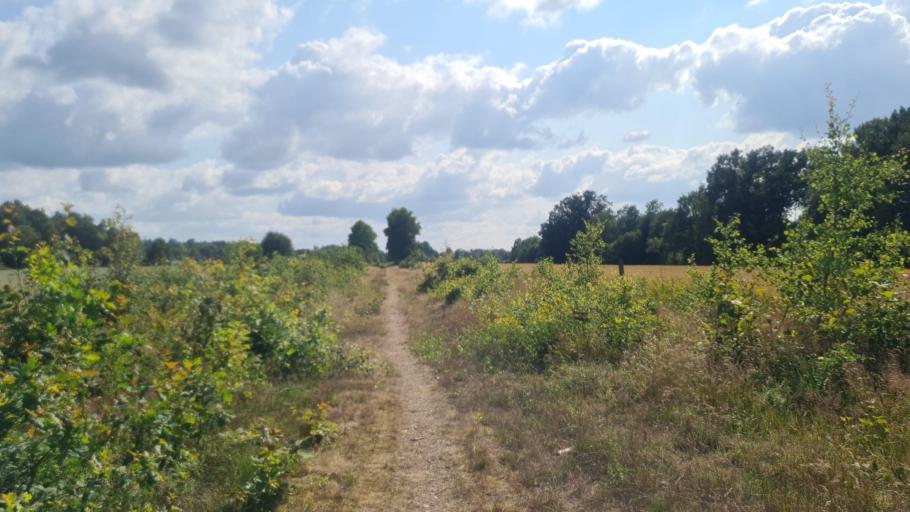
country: SE
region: Kronoberg
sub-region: Ljungby Kommun
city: Ljungby
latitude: 56.7471
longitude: 13.8802
